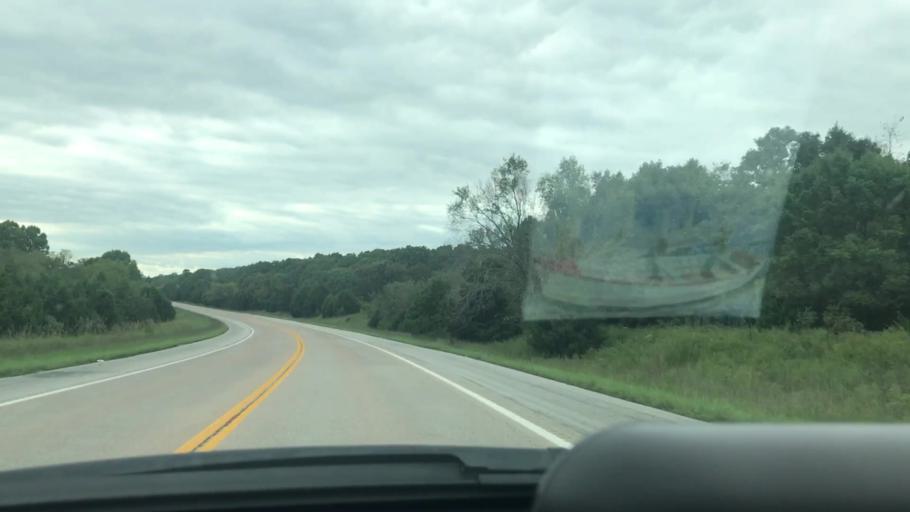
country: US
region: Missouri
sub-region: Benton County
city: Warsaw
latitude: 38.2078
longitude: -93.3300
